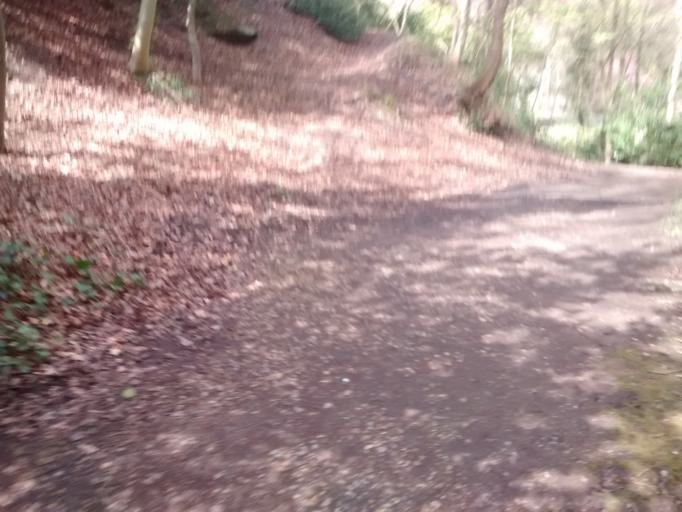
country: GB
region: England
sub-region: County Durham
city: Durham
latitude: 54.7691
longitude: -1.5766
